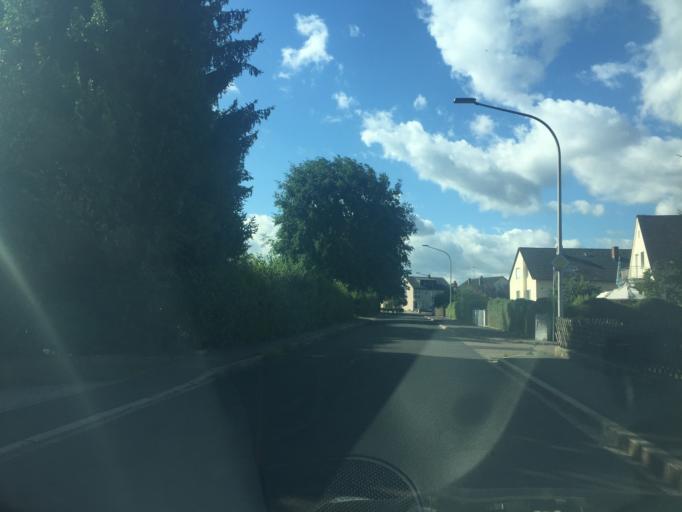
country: DE
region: Bavaria
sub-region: Upper Palatinate
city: Hahnbach
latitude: 49.5335
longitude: 11.8070
